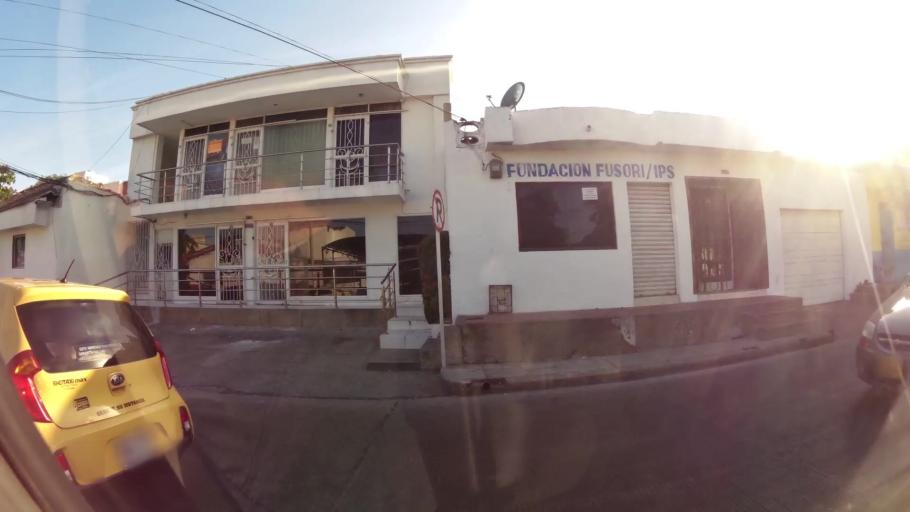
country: CO
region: Atlantico
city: Barranquilla
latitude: 10.9879
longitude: -74.7974
